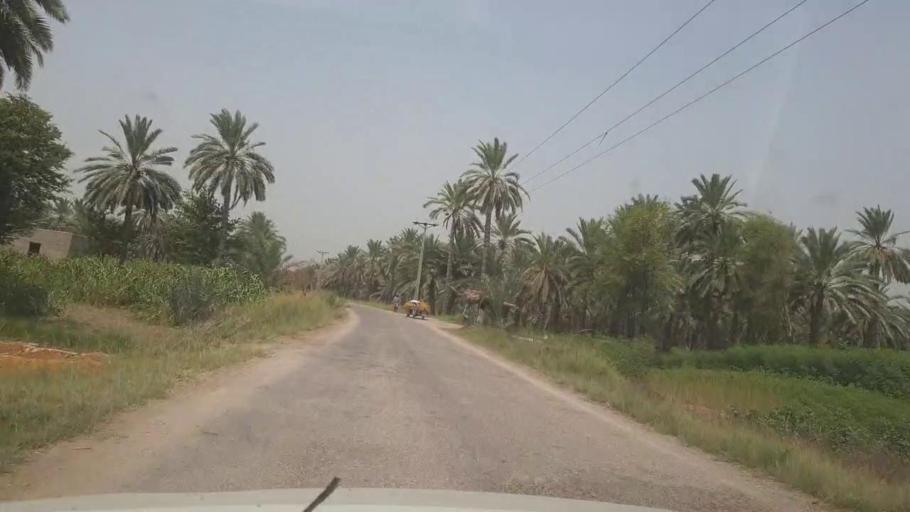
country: PK
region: Sindh
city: Kot Diji
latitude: 27.3625
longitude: 68.6795
